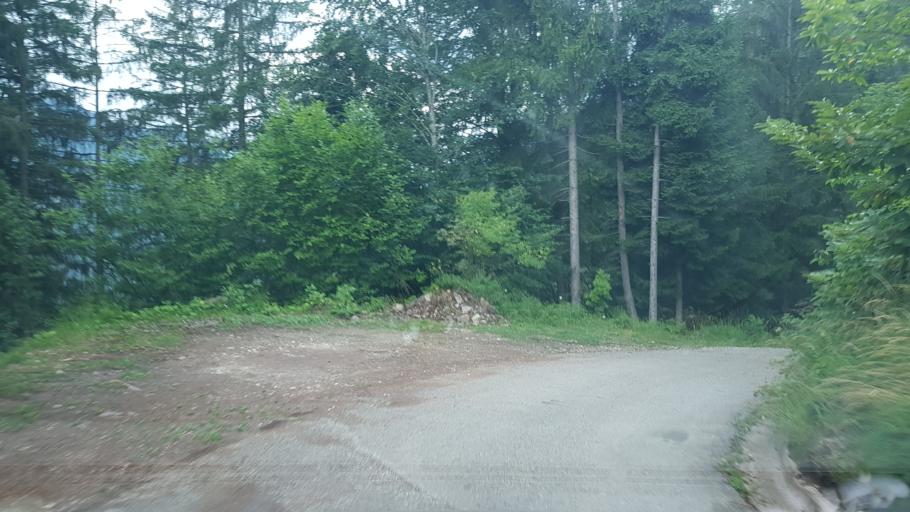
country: IT
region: Friuli Venezia Giulia
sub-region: Provincia di Udine
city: Cercivento
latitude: 46.5347
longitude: 12.9887
